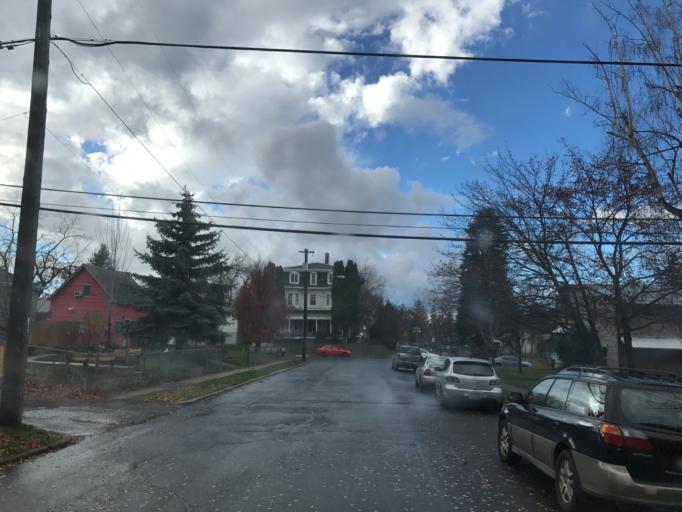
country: US
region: Idaho
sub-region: Latah County
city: Moscow
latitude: 46.7337
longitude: -117.0032
